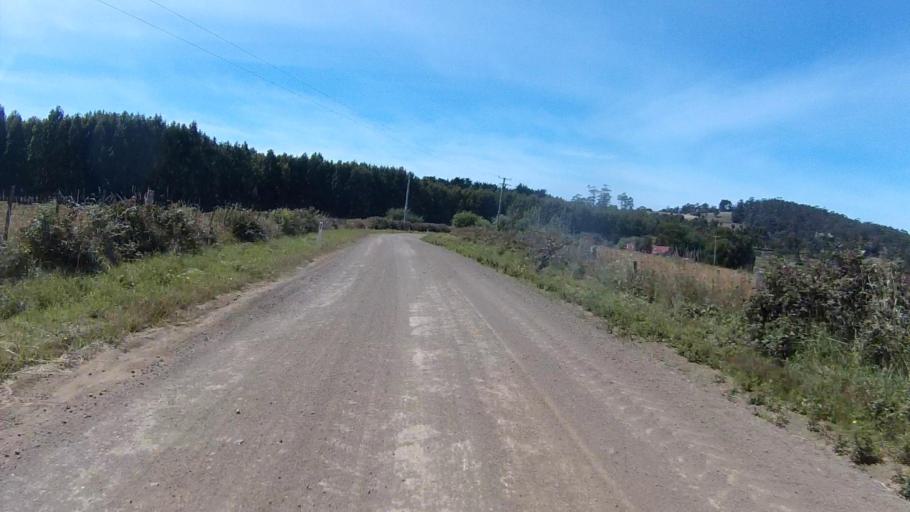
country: AU
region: Tasmania
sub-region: Sorell
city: Sorell
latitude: -42.7103
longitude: 147.7512
